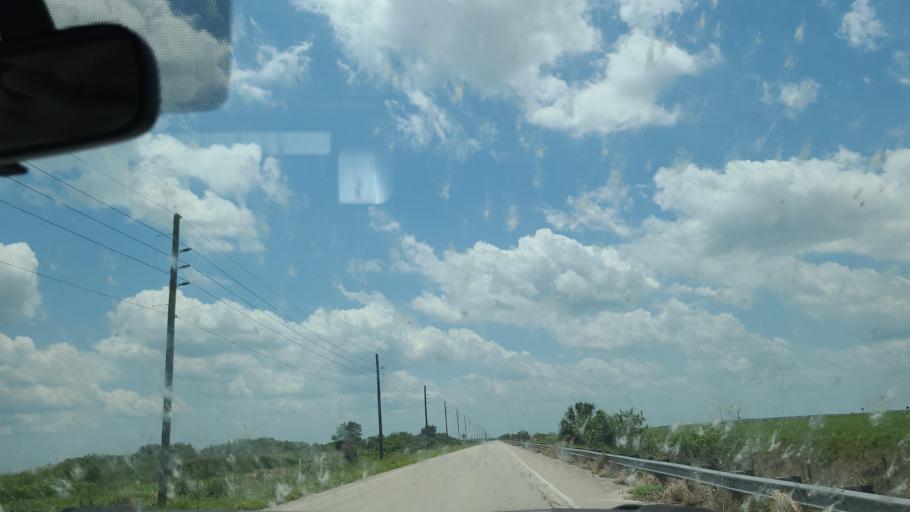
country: US
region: Florida
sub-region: Glades County
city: Buckhead Ridge
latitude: 27.1841
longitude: -81.0943
